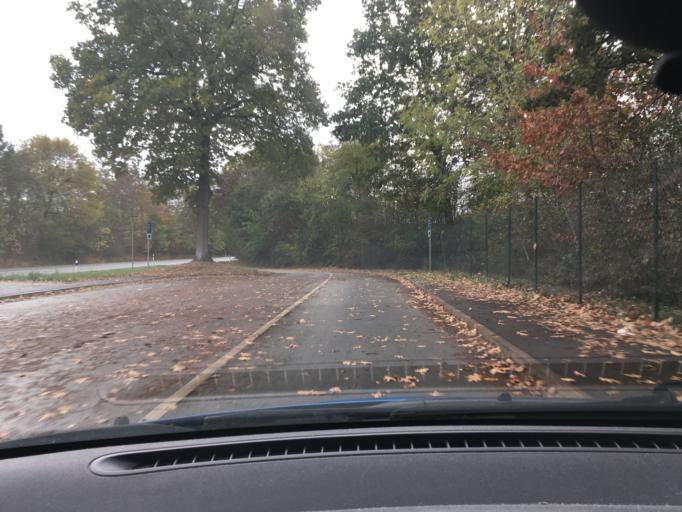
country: DE
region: Schleswig-Holstein
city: Alt Molln
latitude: 53.6169
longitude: 10.6545
